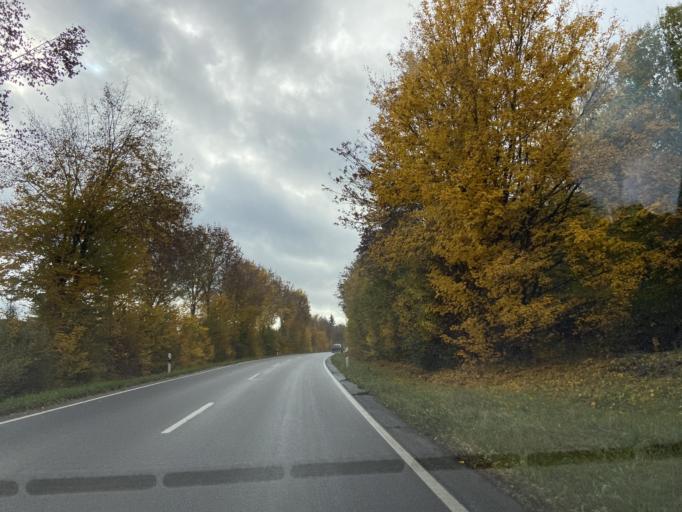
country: DE
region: Baden-Wuerttemberg
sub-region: Tuebingen Region
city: Inzigkofen
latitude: 48.0825
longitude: 9.1993
